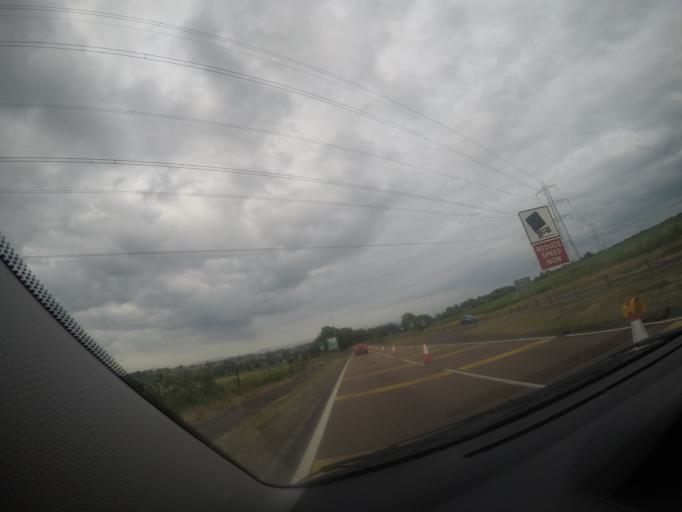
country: GB
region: Scotland
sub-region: Perth and Kinross
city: Perth
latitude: 56.3878
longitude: -3.4920
